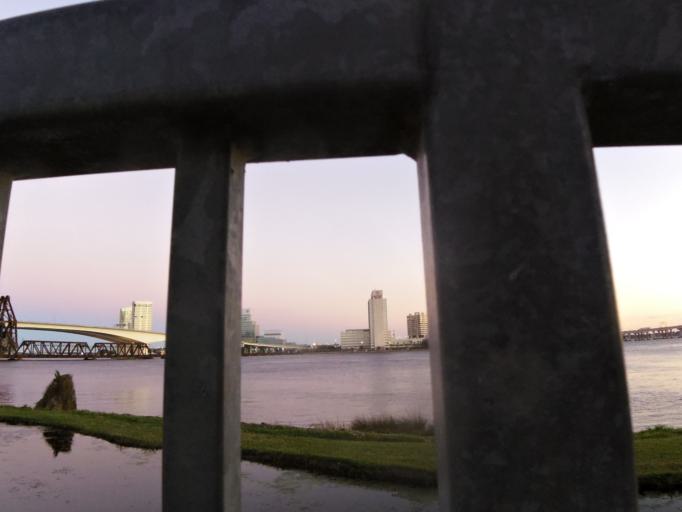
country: US
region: Florida
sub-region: Duval County
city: Jacksonville
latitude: 30.3226
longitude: -81.6704
